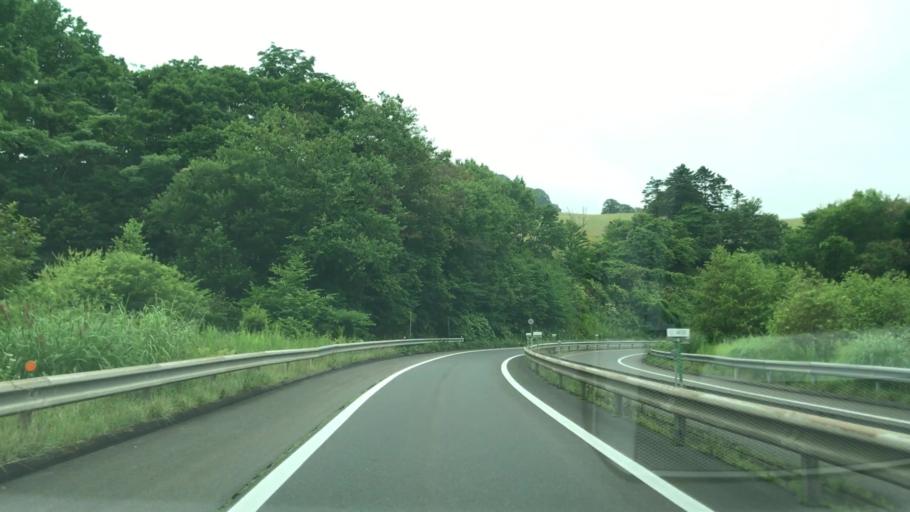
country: JP
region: Hokkaido
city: Muroran
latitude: 42.3991
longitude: 141.0800
